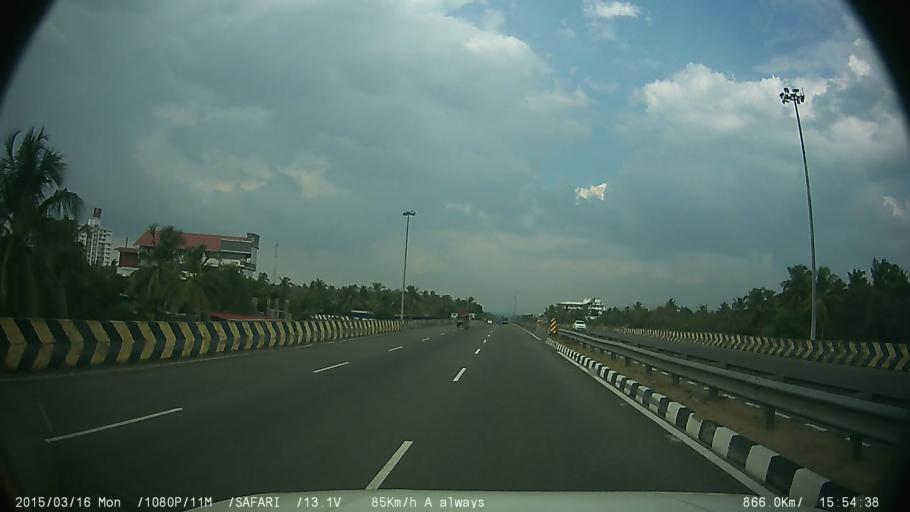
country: IN
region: Kerala
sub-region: Thrissur District
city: Trichur
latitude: 10.4935
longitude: 76.2578
